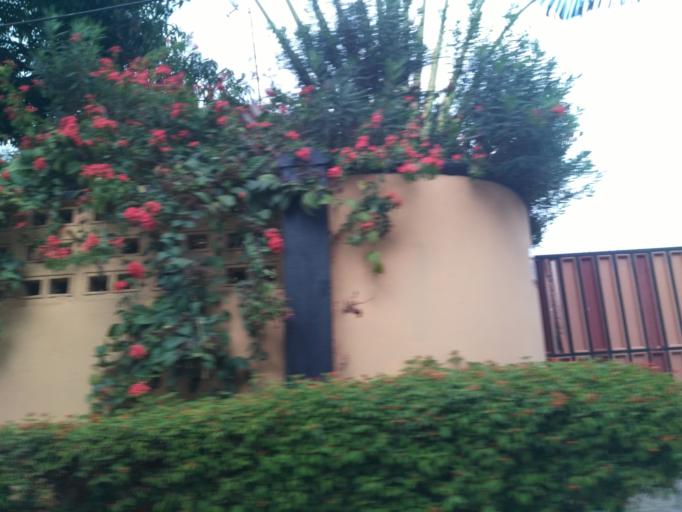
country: TZ
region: Dar es Salaam
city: Magomeni
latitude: -6.7561
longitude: 39.2413
